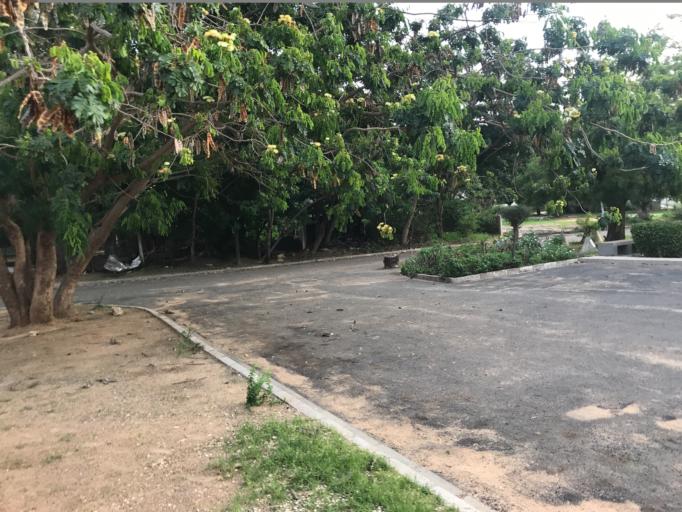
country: SN
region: Dakar
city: Dakar
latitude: 14.6852
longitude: -17.4625
